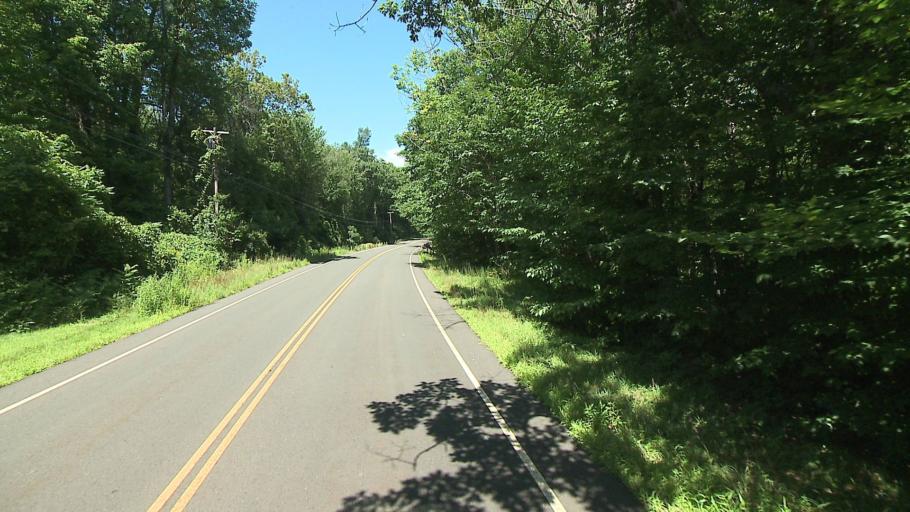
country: US
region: Connecticut
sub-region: Litchfield County
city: Winsted
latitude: 41.9860
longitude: -72.9838
